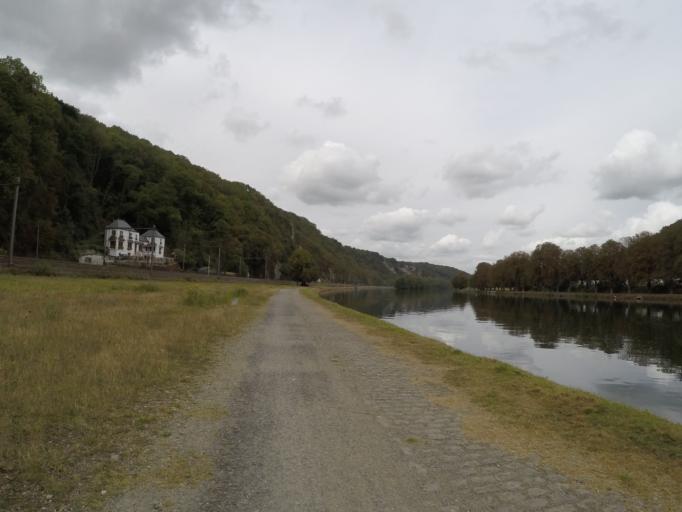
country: BE
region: Wallonia
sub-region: Province de Namur
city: Dinant
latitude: 50.2767
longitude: 4.8952
